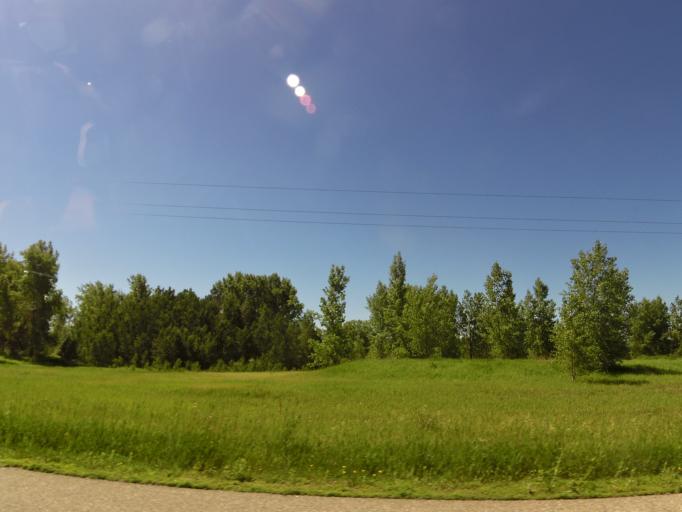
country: US
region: Minnesota
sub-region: Red Lake County
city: Red Lake Falls
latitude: 47.7604
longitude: -96.4105
